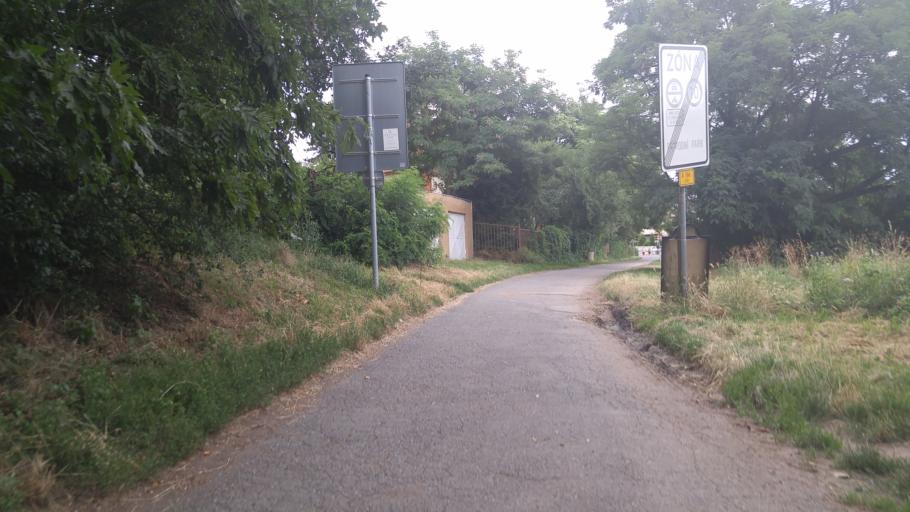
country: CZ
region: Central Bohemia
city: Horomerice
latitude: 50.0990
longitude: 14.3406
